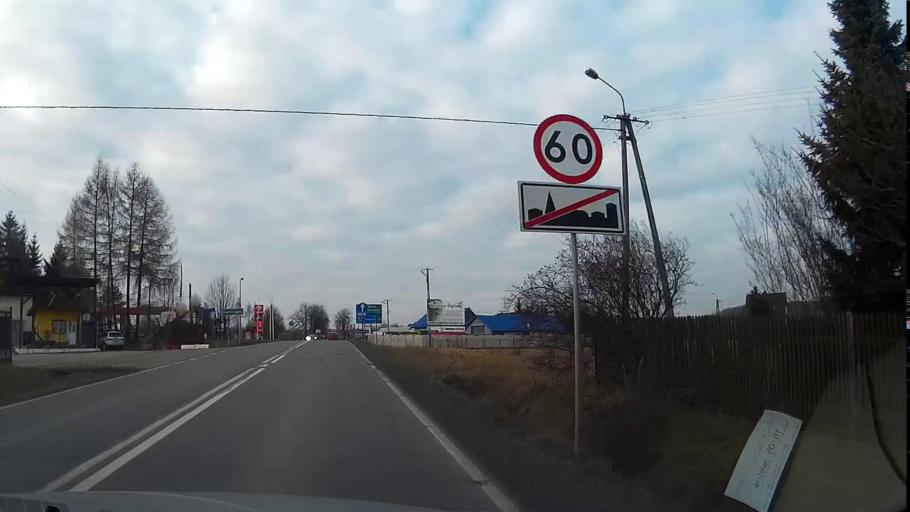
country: PL
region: Lesser Poland Voivodeship
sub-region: Powiat chrzanowski
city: Alwernia
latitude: 50.0599
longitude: 19.5559
